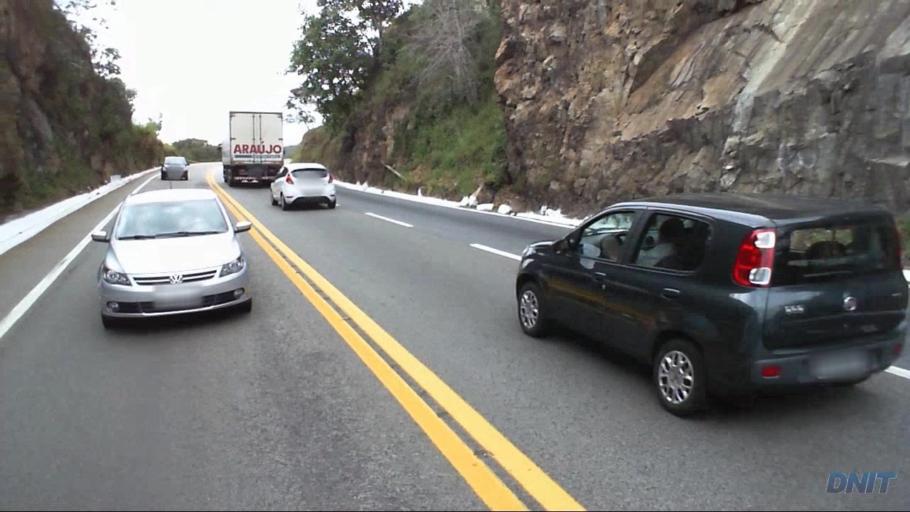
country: BR
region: Minas Gerais
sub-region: Caete
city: Caete
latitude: -19.7867
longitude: -43.7171
